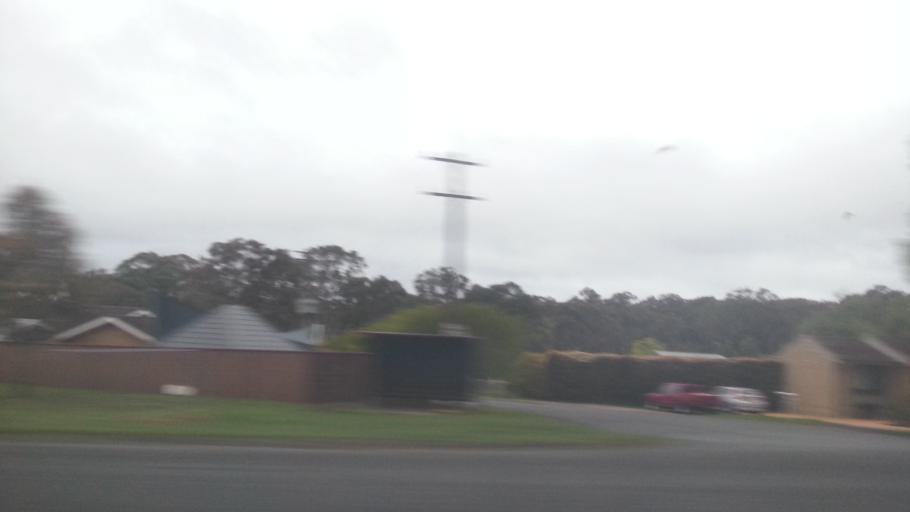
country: AU
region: New South Wales
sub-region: Wollondilly
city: Douglas Park
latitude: -34.2344
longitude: 150.7296
